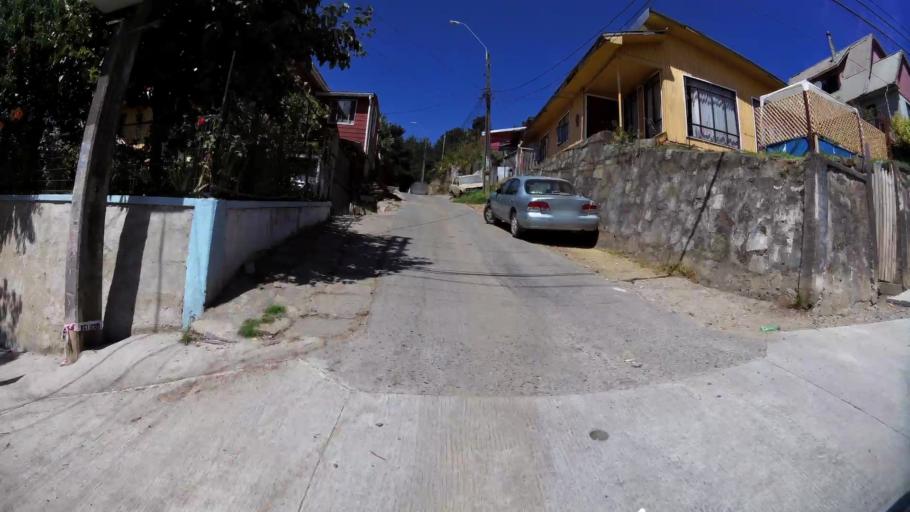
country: CL
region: Biobio
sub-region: Provincia de Concepcion
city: Penco
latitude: -36.7442
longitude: -72.9919
